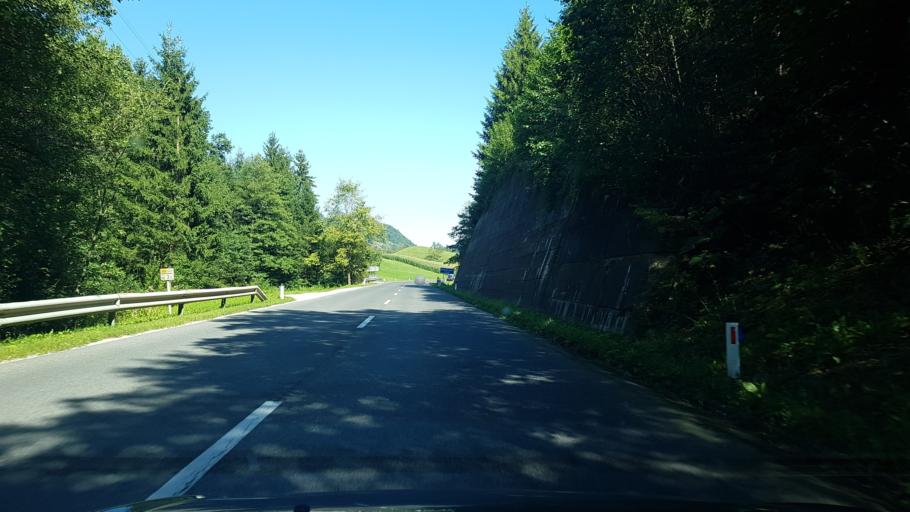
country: SI
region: Sostanj
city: Sostanj
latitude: 46.3607
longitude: 15.0297
